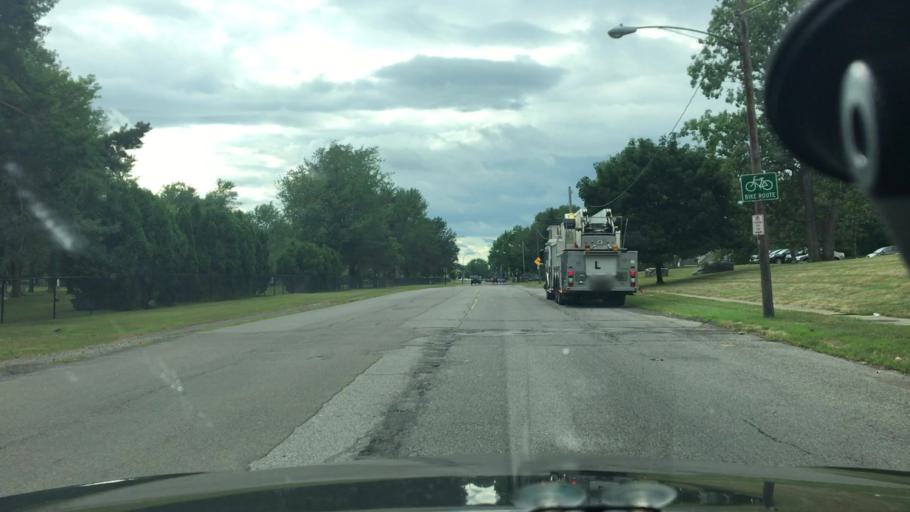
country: US
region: New York
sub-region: Erie County
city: Lackawanna
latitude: 42.8320
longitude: -78.8100
